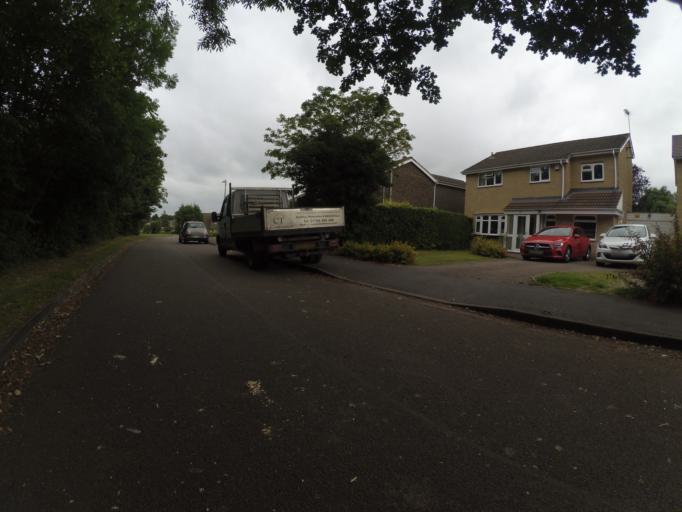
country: GB
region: England
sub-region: Warwickshire
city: Rugby
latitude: 52.3527
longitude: -1.2729
